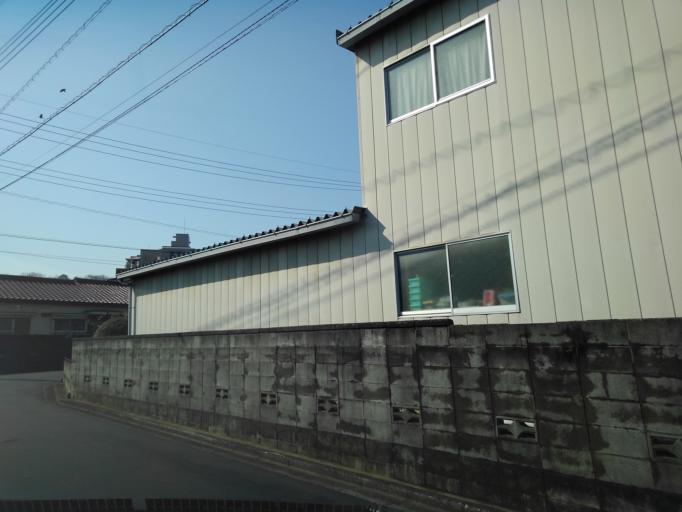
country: JP
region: Saitama
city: Sayama
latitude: 35.7899
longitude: 139.3831
